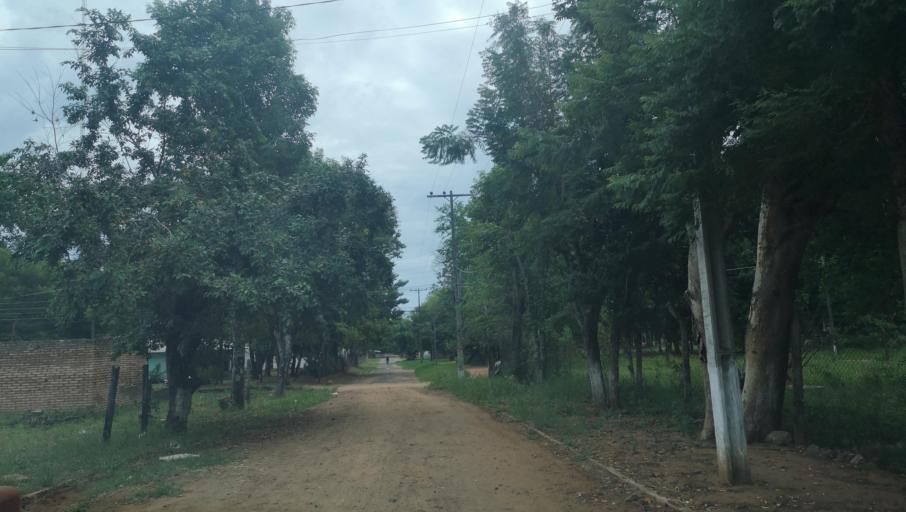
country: PY
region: San Pedro
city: Capiibary
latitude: -24.7274
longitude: -56.0154
